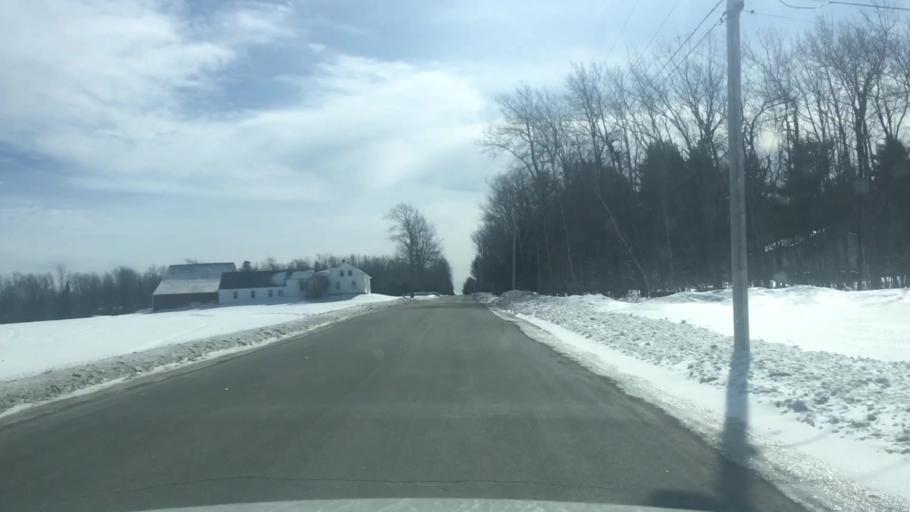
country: US
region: Maine
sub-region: Penobscot County
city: Holden
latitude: 44.7753
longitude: -68.6507
